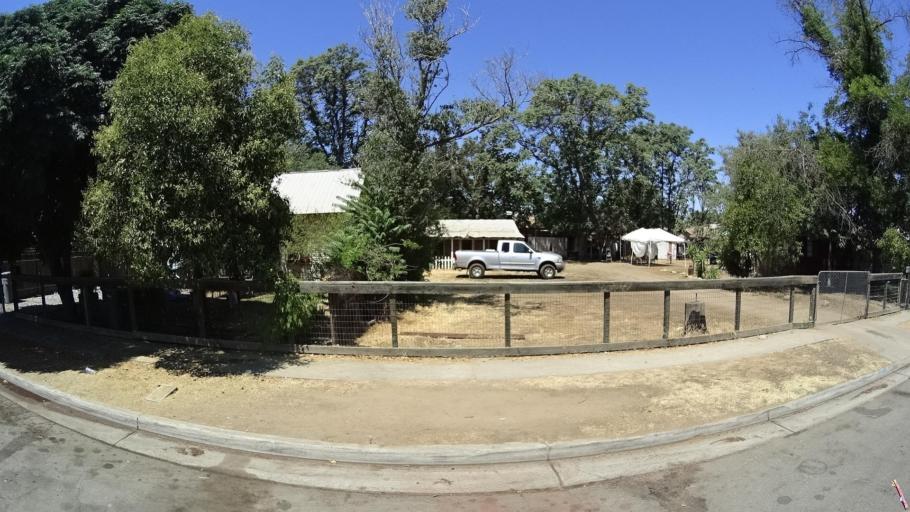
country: US
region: California
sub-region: Fresno County
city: Fresno
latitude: 36.7372
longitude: -119.7393
